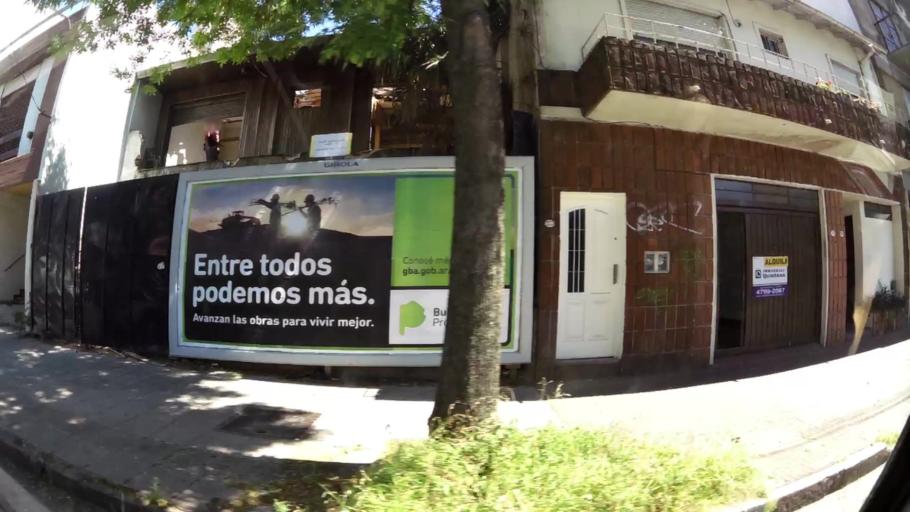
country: AR
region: Buenos Aires
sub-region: Partido de Vicente Lopez
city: Olivos
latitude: -34.5168
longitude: -58.4971
